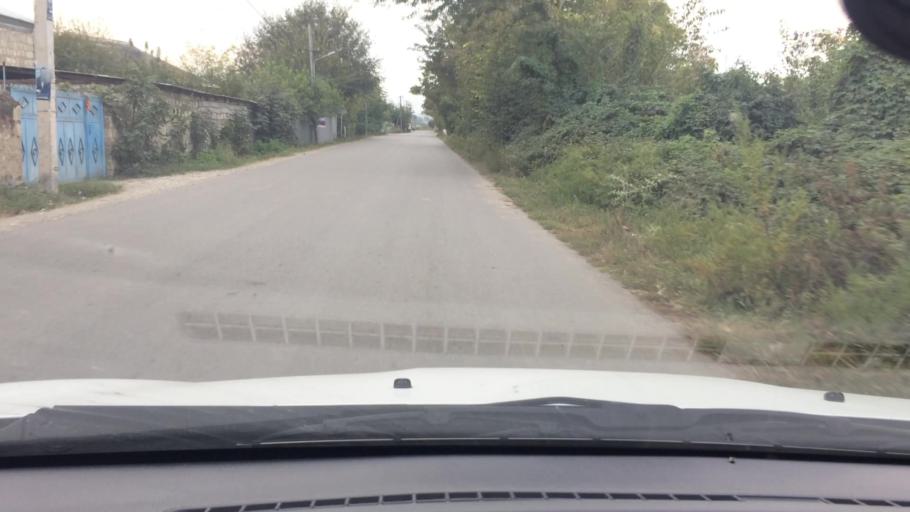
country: AM
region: Tavush
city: Bagratashen
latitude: 41.3387
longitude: 44.9246
